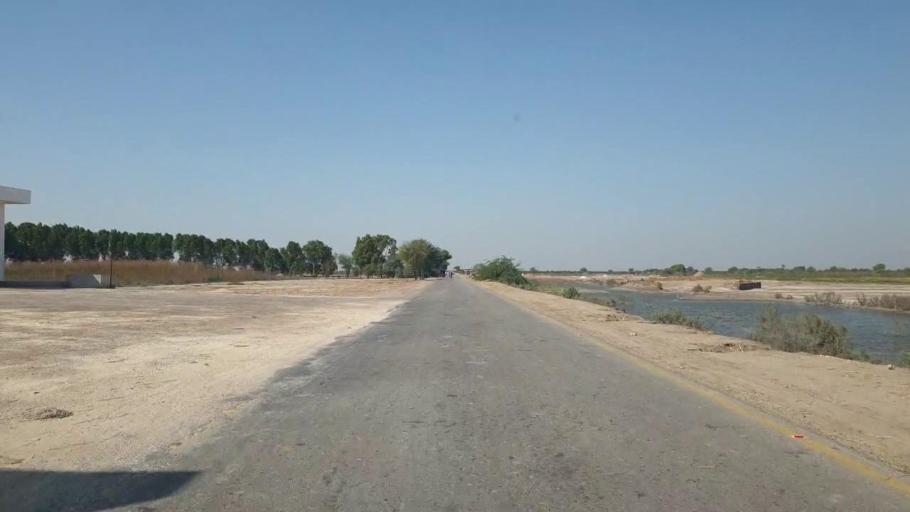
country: PK
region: Sindh
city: Rajo Khanani
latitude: 25.0071
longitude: 68.8360
